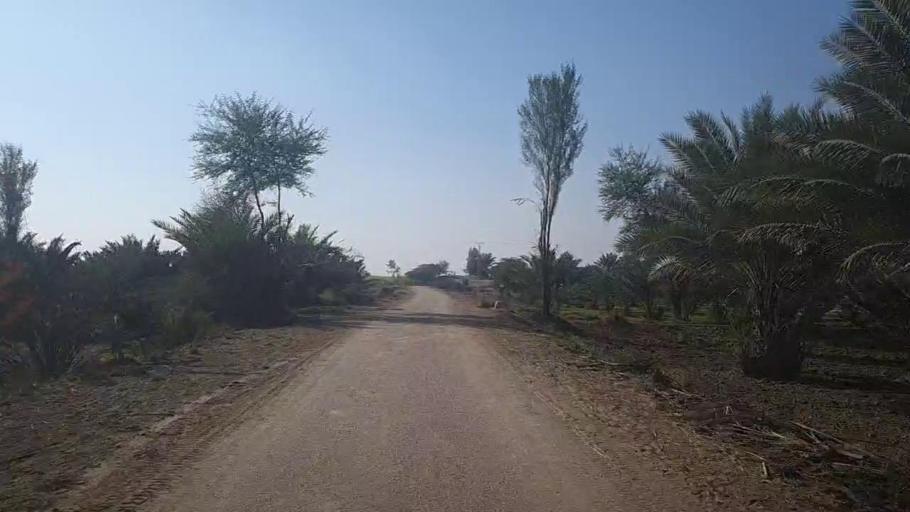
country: PK
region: Sindh
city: Khairpur
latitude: 27.4412
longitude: 68.7308
